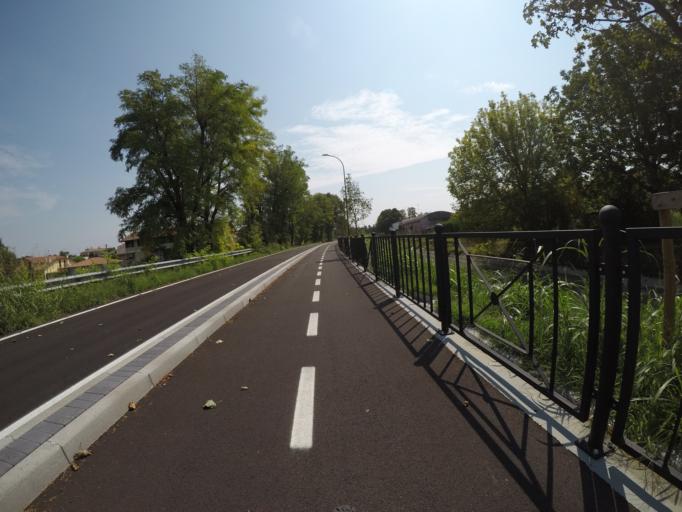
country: IT
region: Veneto
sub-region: Provincia di Rovigo
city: Lendinara
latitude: 45.0856
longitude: 11.5909
